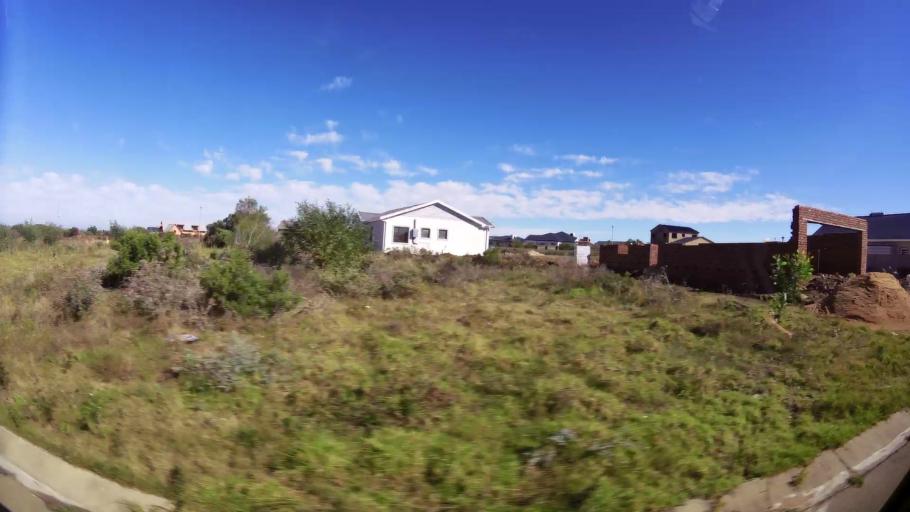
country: ZA
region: Eastern Cape
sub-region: Cacadu District Municipality
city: Jeffrey's Bay
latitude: -34.0371
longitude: 24.9082
